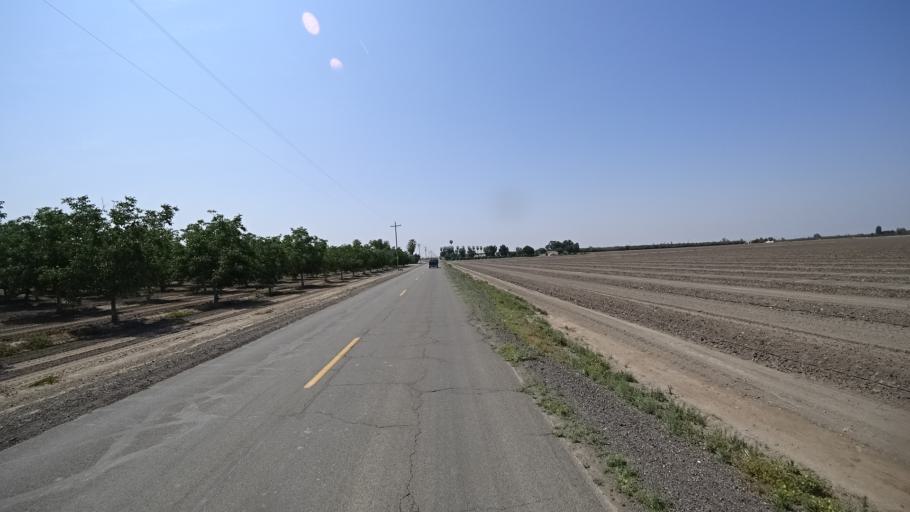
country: US
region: California
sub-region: Kings County
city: Armona
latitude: 36.3479
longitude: -119.7449
